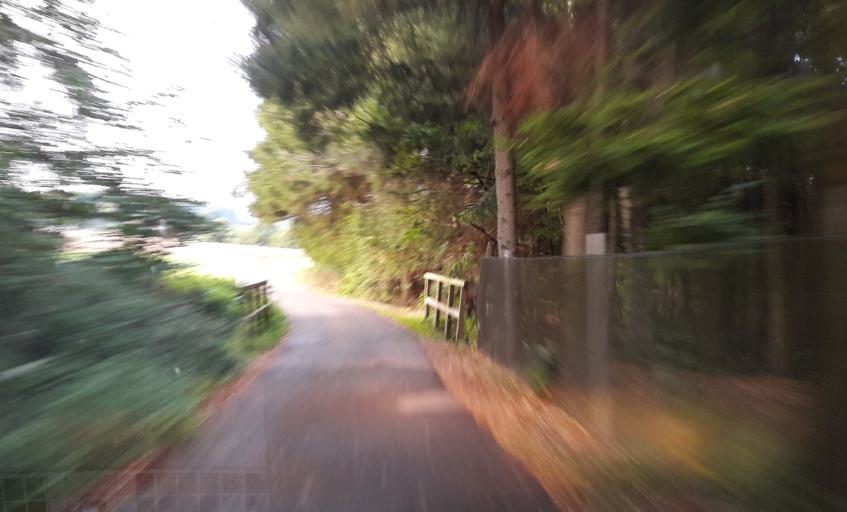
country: DE
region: Rheinland-Pfalz
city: Breitenbach
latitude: 49.4431
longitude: 7.2285
